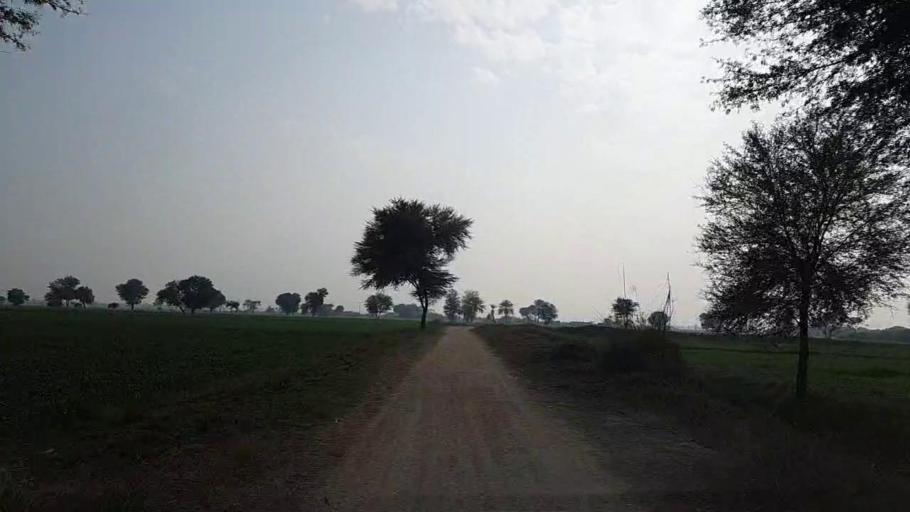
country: PK
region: Sindh
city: Nawabshah
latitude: 26.2835
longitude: 68.4456
